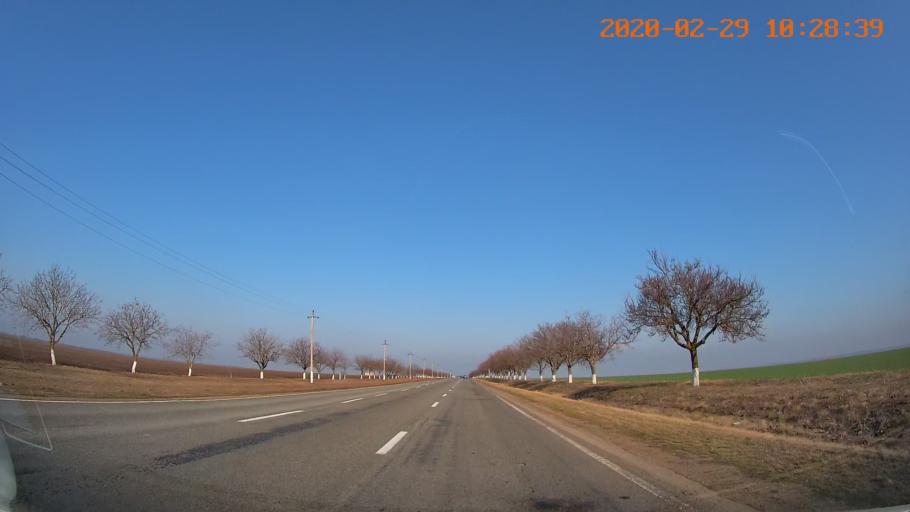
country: MD
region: Telenesti
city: Tiraspolul Nou
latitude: 46.9136
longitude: 29.5901
